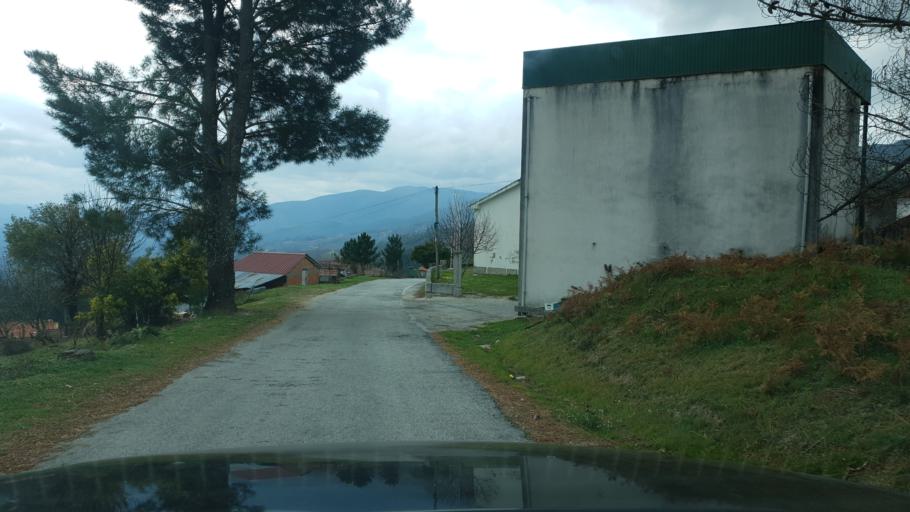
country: PT
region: Viseu
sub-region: Castro Daire
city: Castro Daire
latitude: 40.8795
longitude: -8.0109
